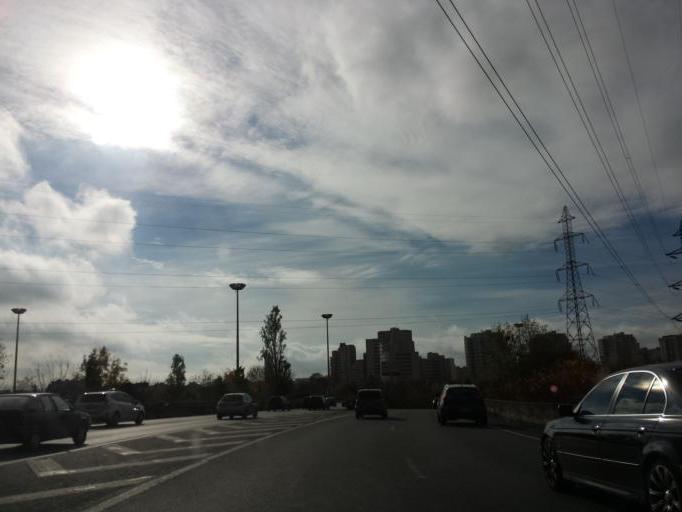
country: FR
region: Ile-de-France
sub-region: Departement des Hauts-de-Seine
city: Gennevilliers
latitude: 48.9388
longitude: 2.2943
